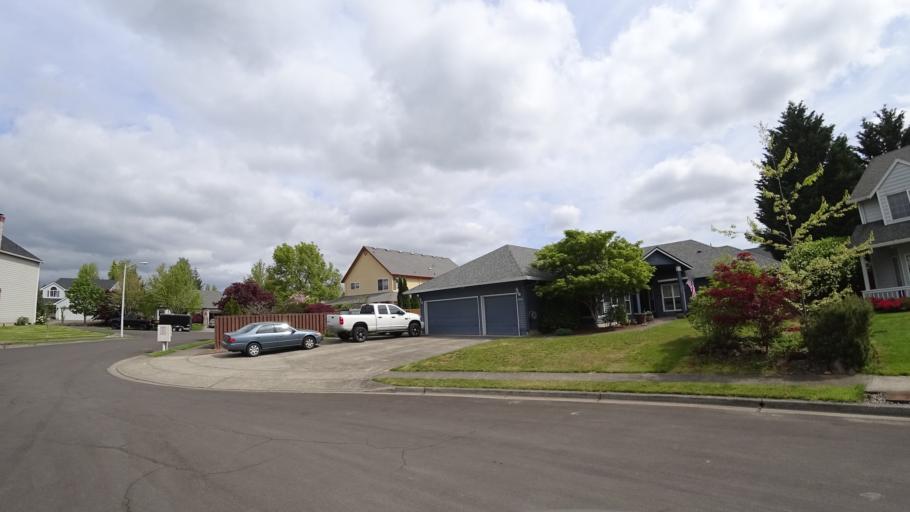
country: US
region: Oregon
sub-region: Washington County
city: Hillsboro
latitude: 45.5453
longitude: -122.9880
